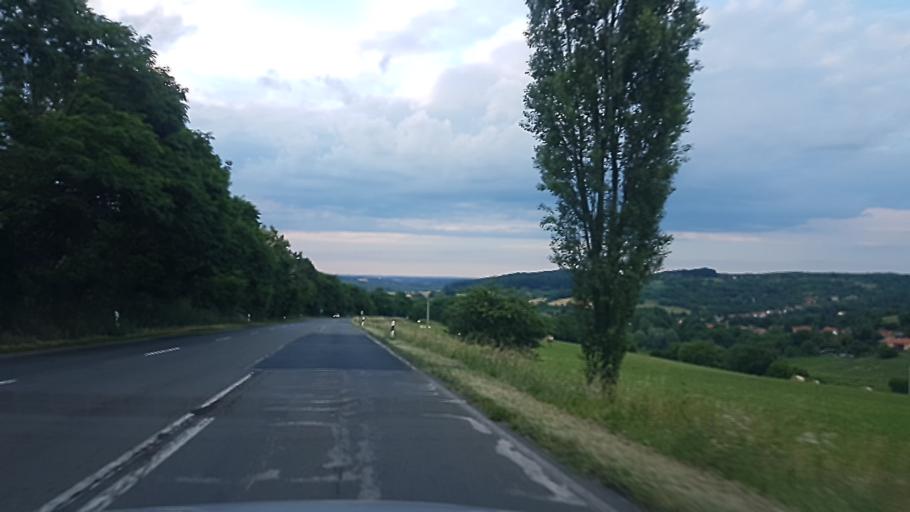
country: HU
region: Somogy
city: Kaposvar
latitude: 46.2742
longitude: 17.8224
